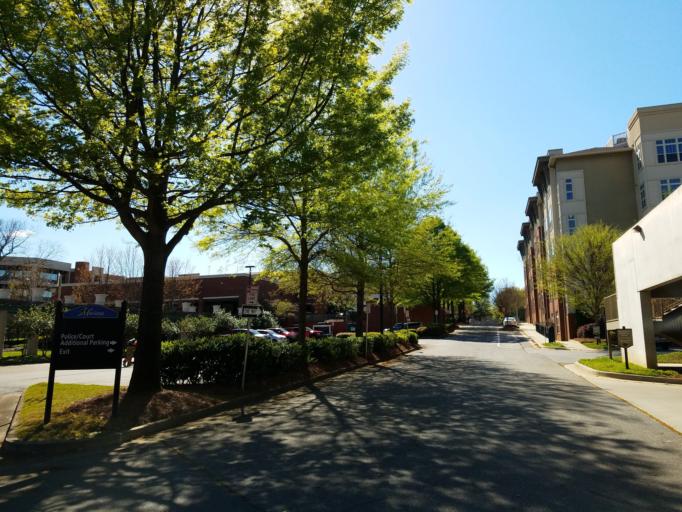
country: US
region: Georgia
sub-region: Cobb County
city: Marietta
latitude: 33.9546
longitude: -84.5456
